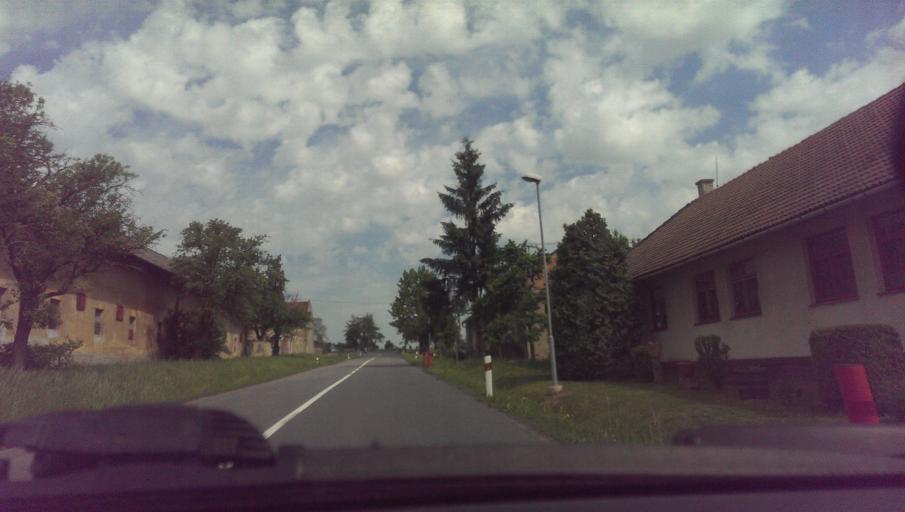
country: CZ
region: Zlin
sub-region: Okres Zlin
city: Otrokovice
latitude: 49.2358
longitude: 17.5383
